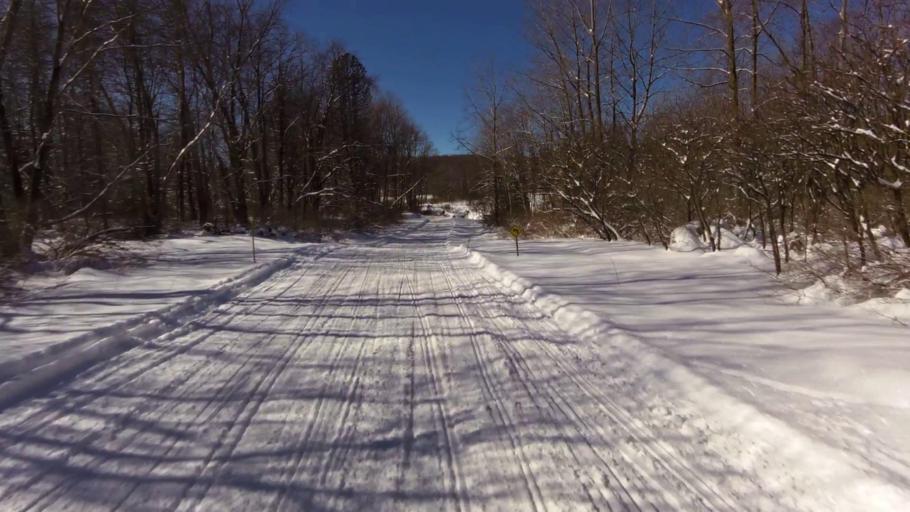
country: US
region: New York
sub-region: Chautauqua County
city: Mayville
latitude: 42.2479
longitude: -79.4378
